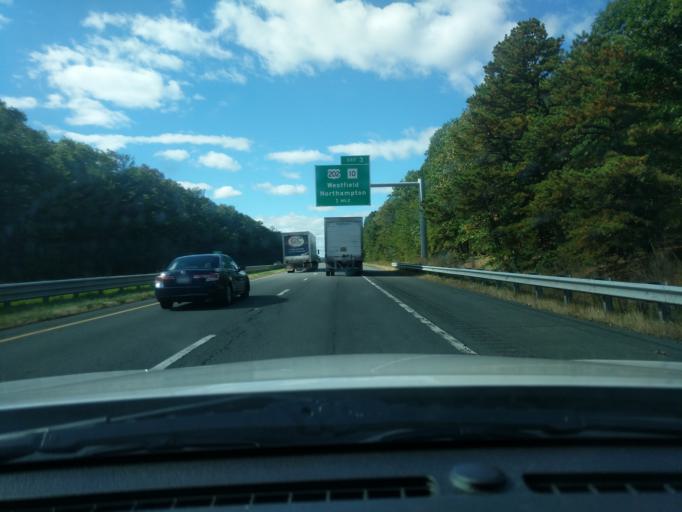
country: US
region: Massachusetts
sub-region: Hampden County
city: Westfield
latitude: 42.1406
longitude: -72.7132
